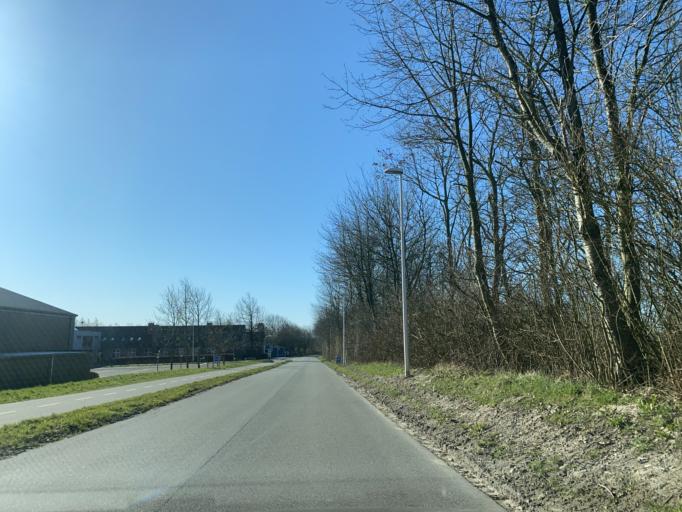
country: DK
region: Central Jutland
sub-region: Skanderborg Kommune
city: Skovby
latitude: 56.1910
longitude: 9.9636
